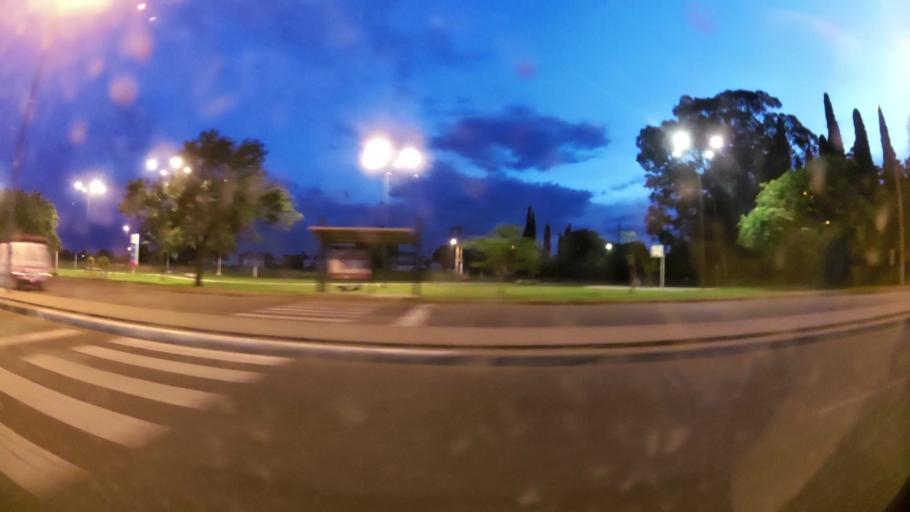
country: AR
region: Buenos Aires
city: San Nicolas de los Arroyos
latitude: -33.3516
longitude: -60.2385
